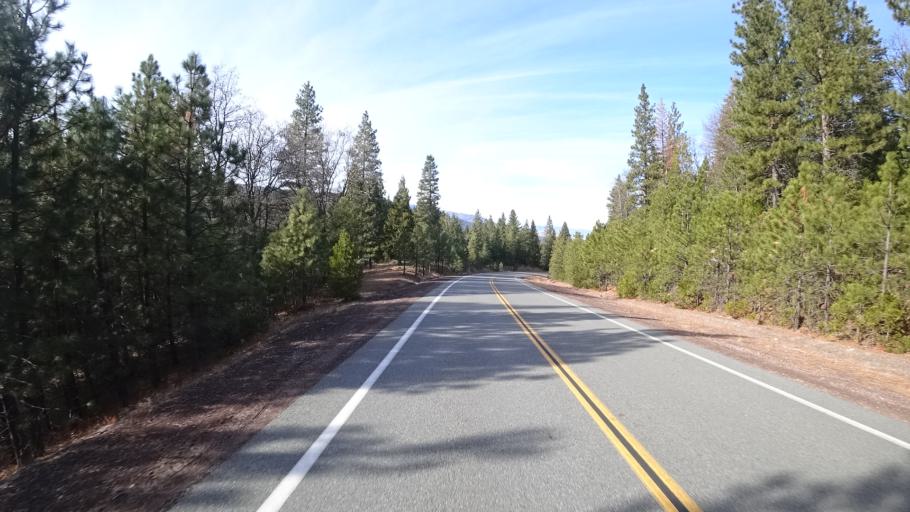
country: US
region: California
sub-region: Siskiyou County
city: Weed
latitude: 41.3904
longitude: -122.4115
